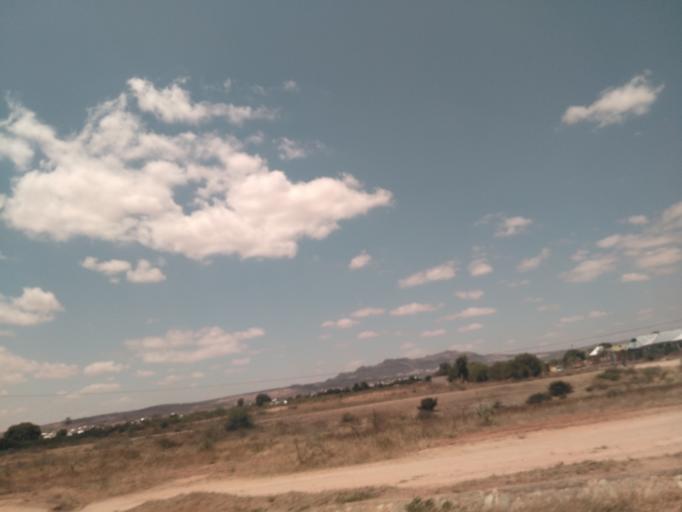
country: TZ
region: Dodoma
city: Kisasa
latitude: -6.1698
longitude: 35.7748
